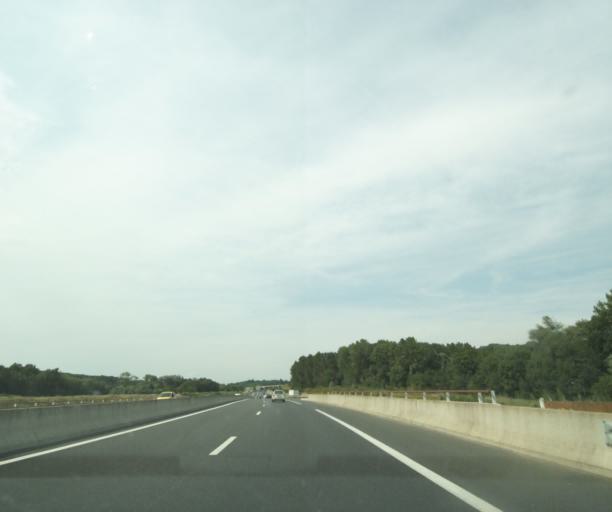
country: FR
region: Centre
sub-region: Departement d'Indre-et-Loire
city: La Membrolle-sur-Choisille
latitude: 47.4171
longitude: 0.6359
